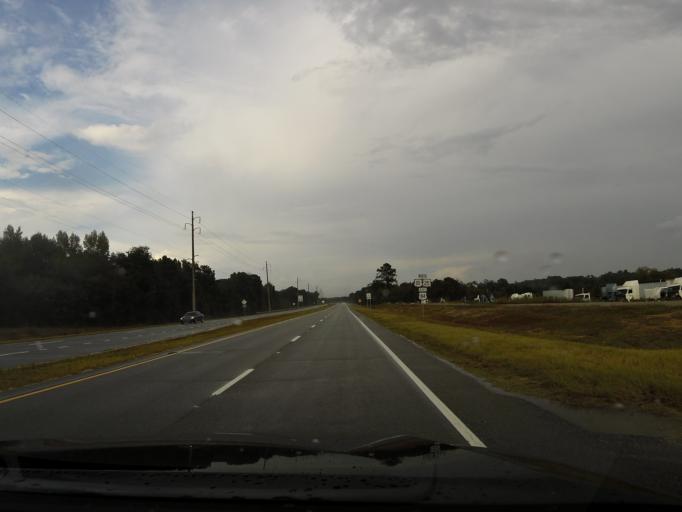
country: US
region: Georgia
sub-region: Long County
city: Ludowici
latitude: 31.6788
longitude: -81.8150
